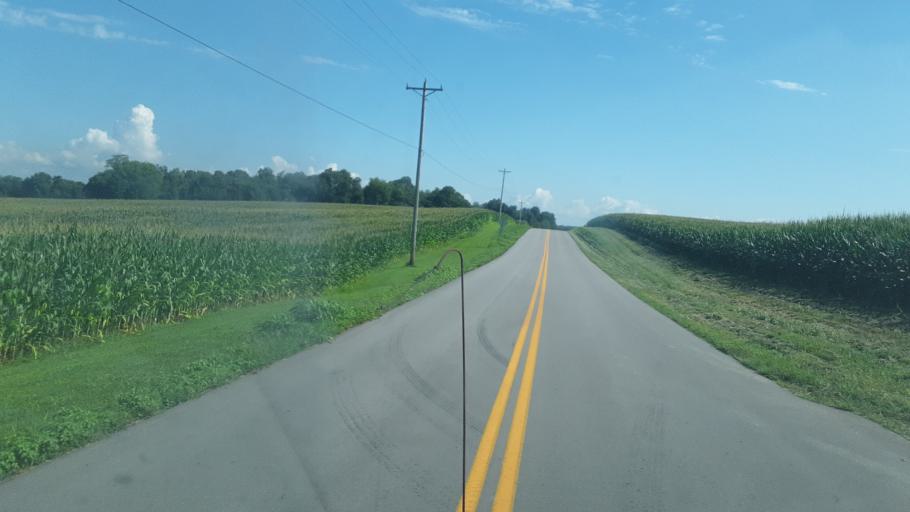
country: US
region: Kentucky
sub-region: Todd County
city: Elkton
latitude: 36.7490
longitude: -87.2249
